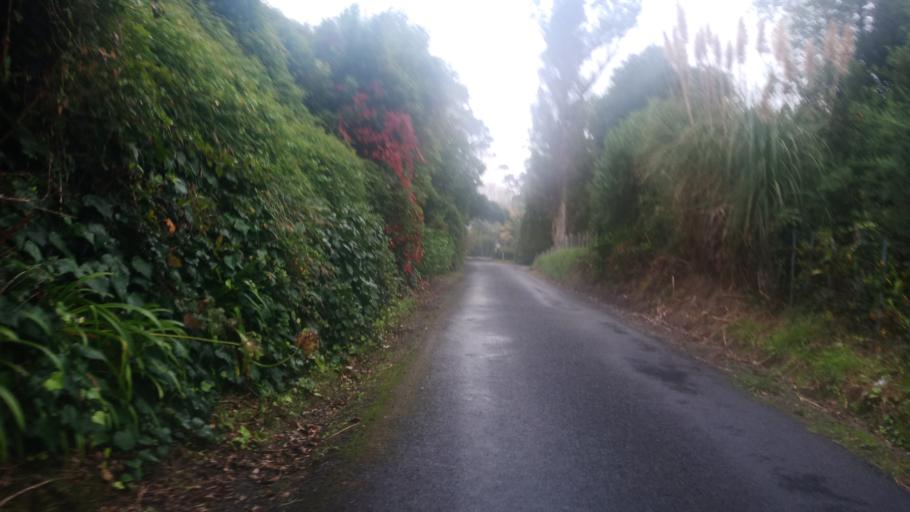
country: NZ
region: Gisborne
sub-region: Gisborne District
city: Gisborne
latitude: -38.6545
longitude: 178.0359
